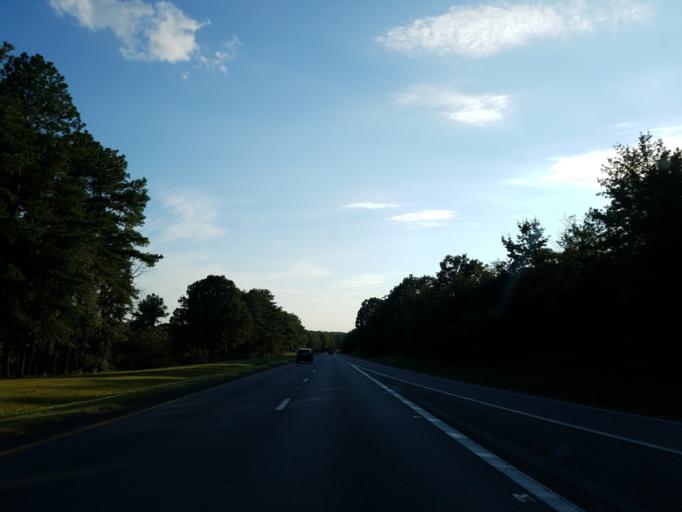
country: US
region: North Carolina
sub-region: Cleveland County
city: White Plains
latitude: 35.1773
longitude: -81.4170
